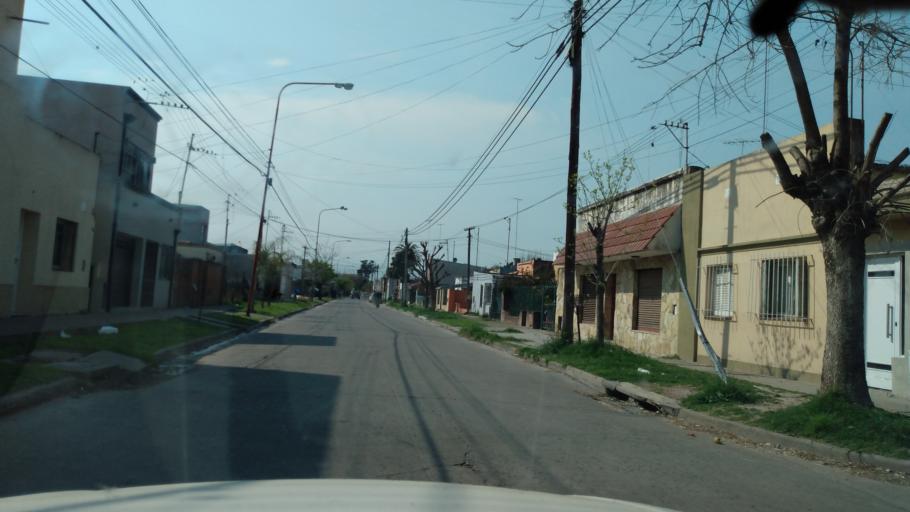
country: AR
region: Buenos Aires
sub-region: Partido de Lujan
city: Lujan
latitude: -34.5725
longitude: -59.1184
